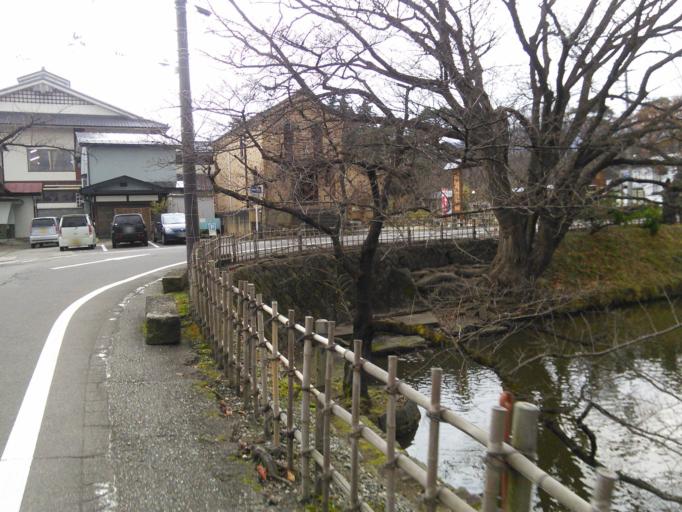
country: JP
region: Fukushima
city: Kitakata
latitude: 37.4898
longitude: 139.9310
